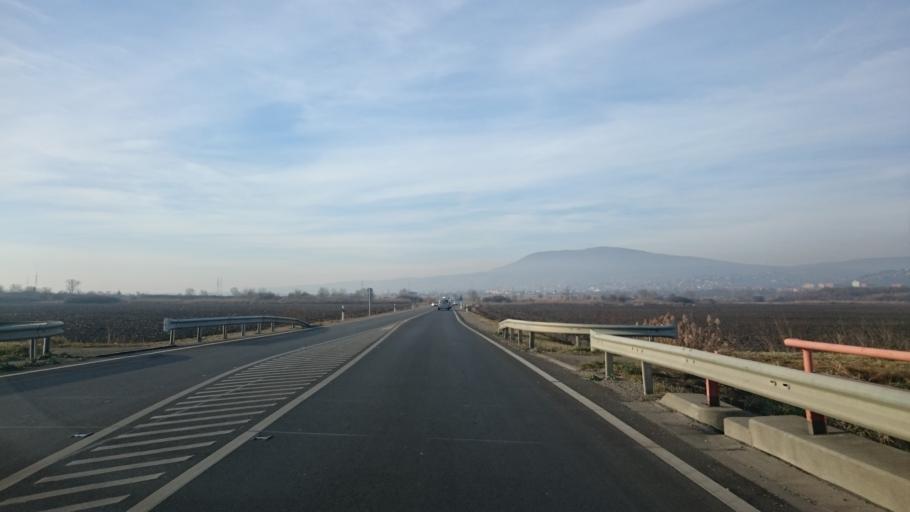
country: HU
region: Baranya
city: Pecs
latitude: 46.0489
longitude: 18.2051
